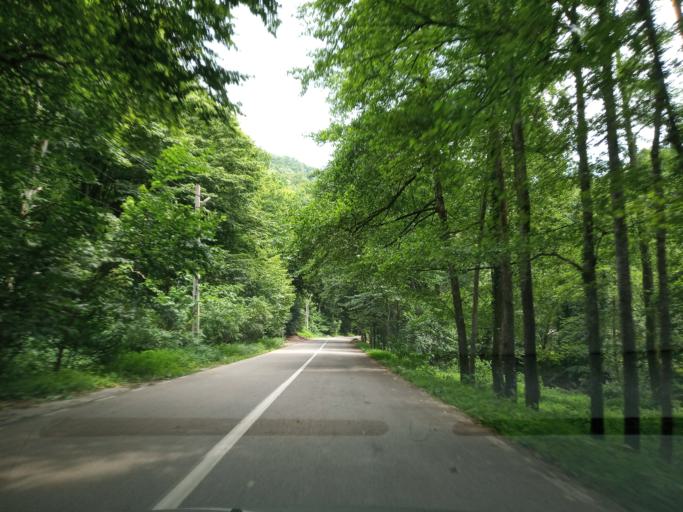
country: RO
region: Gorj
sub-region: Comuna Tismana
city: Pocruia
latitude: 45.0818
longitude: 22.9262
